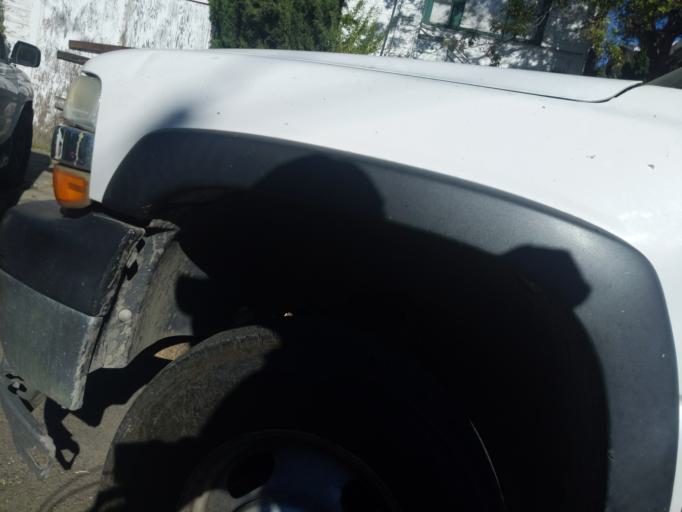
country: US
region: California
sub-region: Alameda County
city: Alameda
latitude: 37.7859
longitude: -122.2206
